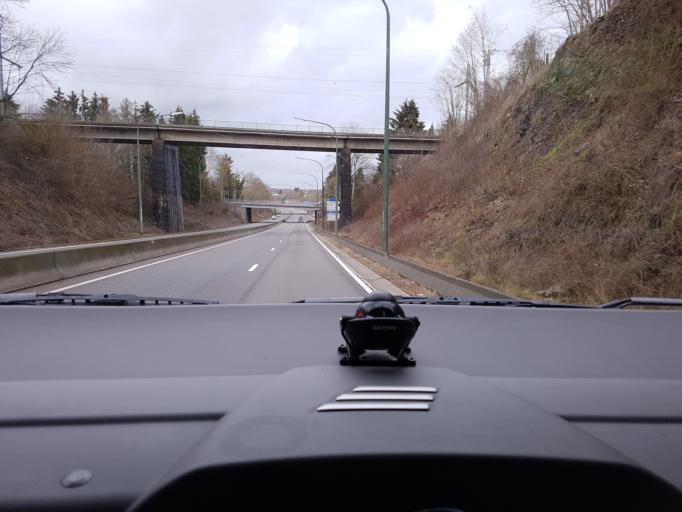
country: BE
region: Wallonia
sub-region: Province du Luxembourg
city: Marche-en-Famenne
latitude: 50.2199
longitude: 5.3428
